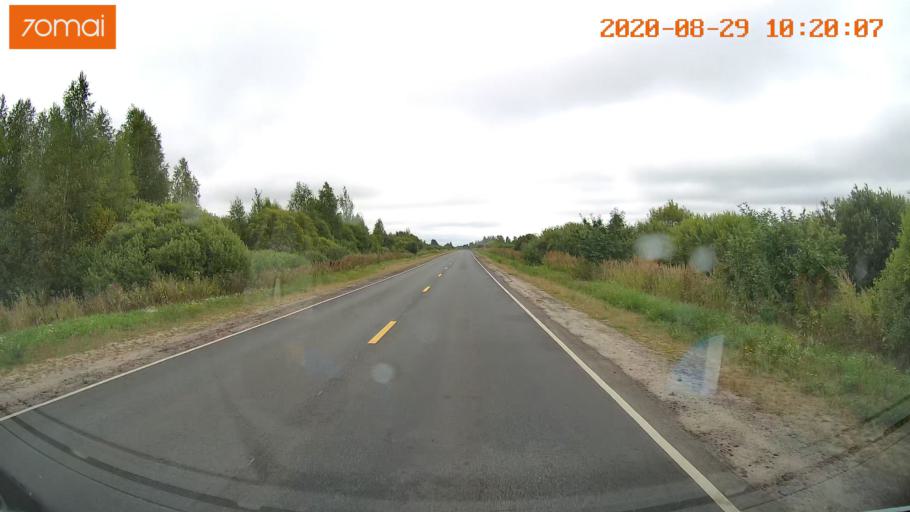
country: RU
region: Ivanovo
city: Yur'yevets
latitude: 57.3250
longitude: 42.8767
